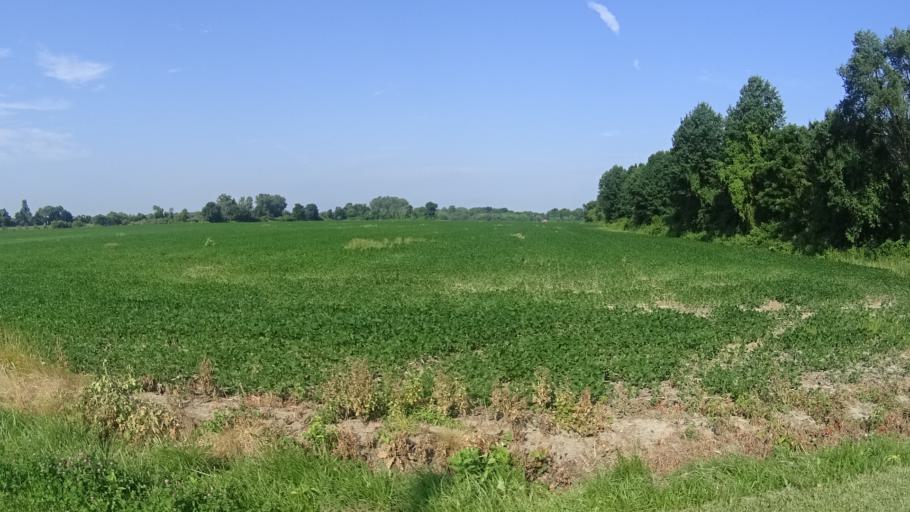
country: US
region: Ohio
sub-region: Lorain County
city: Vermilion
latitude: 41.3835
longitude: -82.4431
